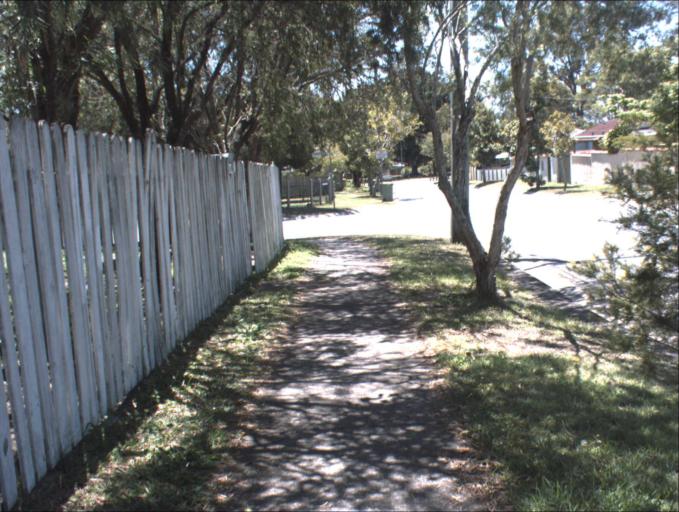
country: AU
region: Queensland
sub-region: Logan
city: Woodridge
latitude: -27.6247
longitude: 153.1077
